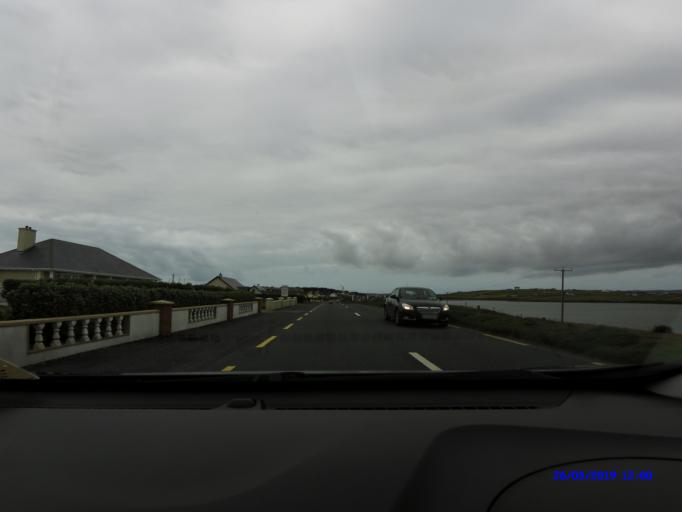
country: IE
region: Connaught
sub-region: Maigh Eo
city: Belmullet
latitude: 54.2158
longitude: -9.9682
